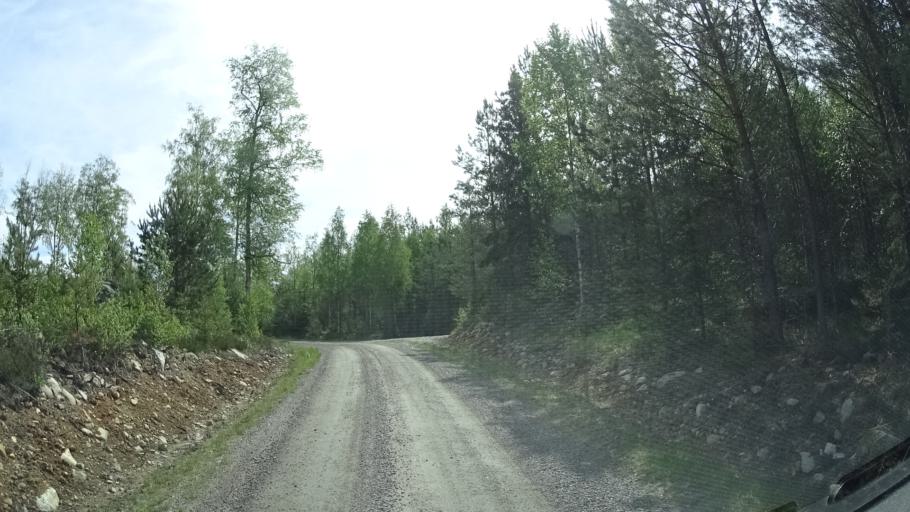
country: SE
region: OEstergoetland
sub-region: Finspangs Kommun
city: Finspang
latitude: 58.7789
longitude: 15.8632
